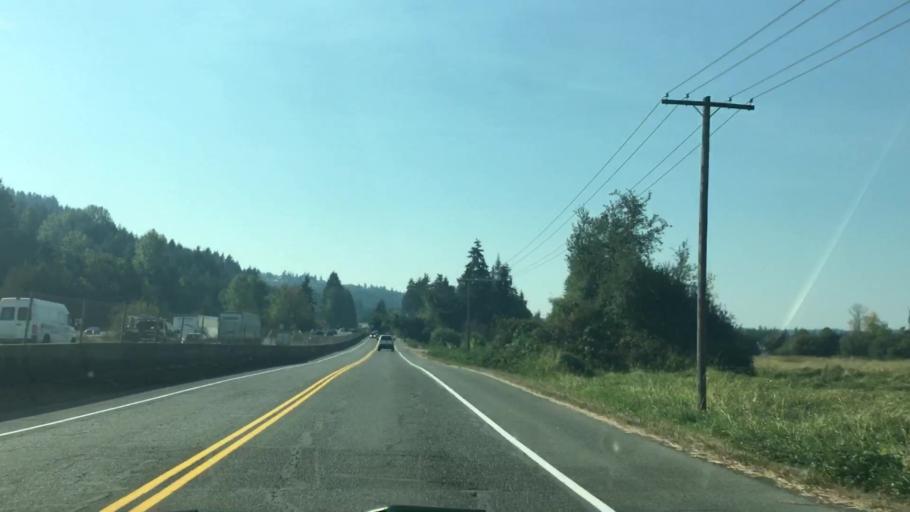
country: US
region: Washington
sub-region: King County
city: West Lake Sammamish
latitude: 47.5507
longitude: -122.0728
